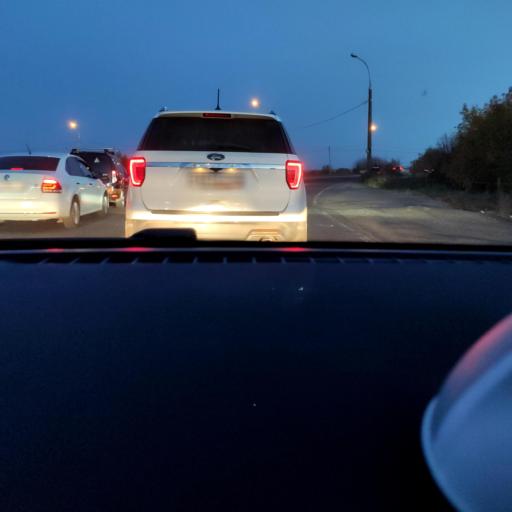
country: RU
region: Samara
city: Samara
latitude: 53.1266
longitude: 50.1694
